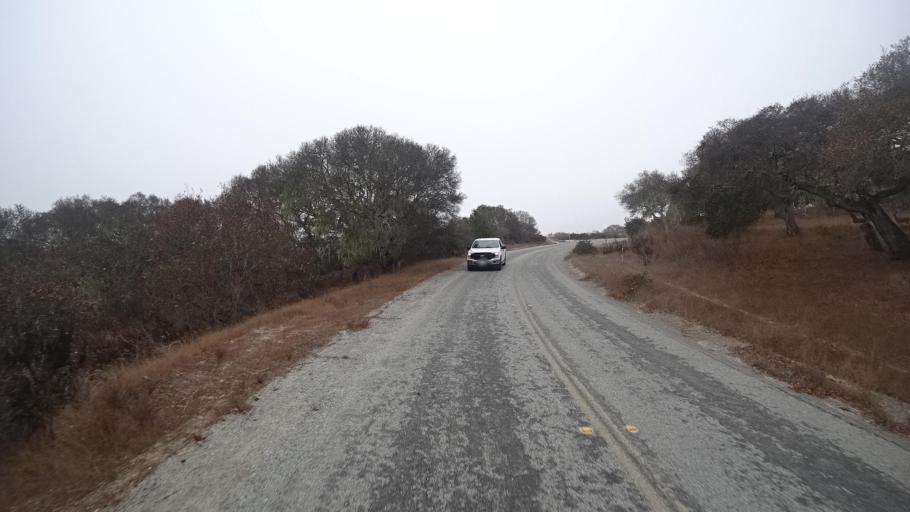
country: US
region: California
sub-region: Monterey County
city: Boronda
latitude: 36.6448
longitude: -121.7302
